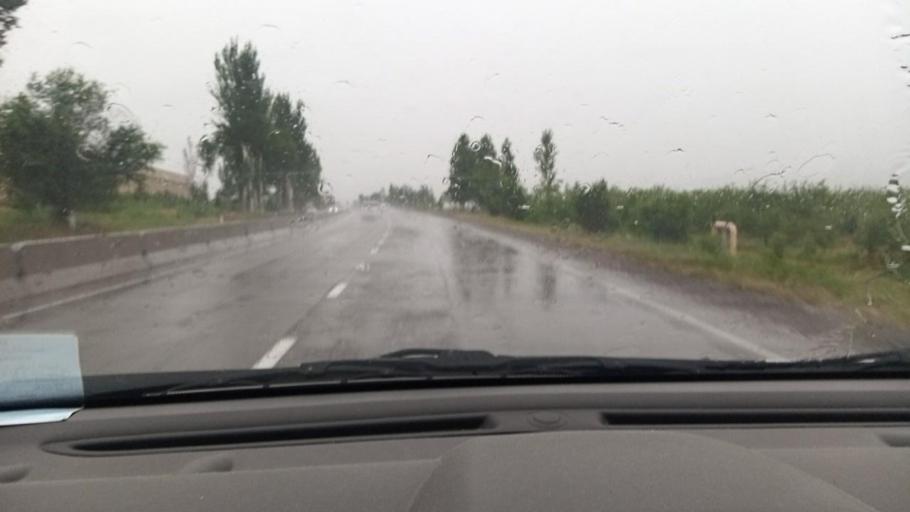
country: UZ
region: Toshkent
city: Angren
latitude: 40.9712
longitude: 69.9901
